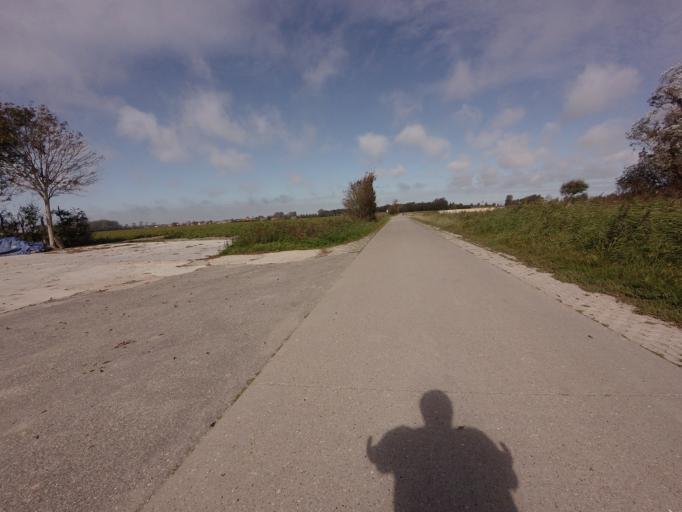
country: NL
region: Zeeland
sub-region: Gemeente Vlissingen
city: Vlissingen
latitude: 51.5099
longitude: 3.5265
